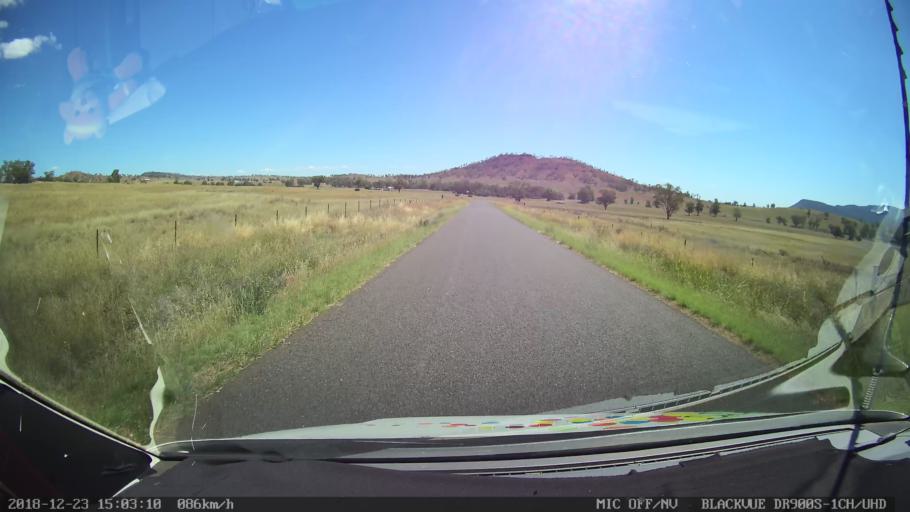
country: AU
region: New South Wales
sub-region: Tamworth Municipality
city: Manilla
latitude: -30.7360
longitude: 150.7677
